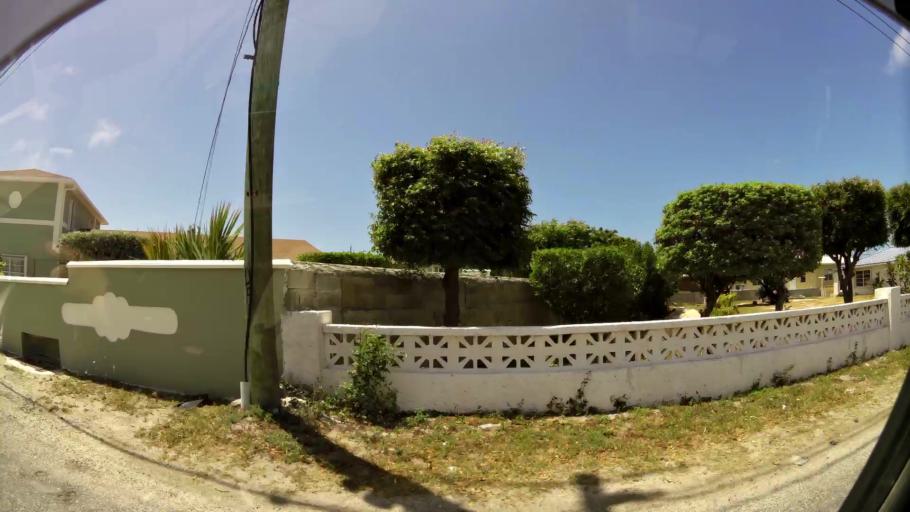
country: TC
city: Cockburn Town
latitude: 21.4504
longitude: -71.1476
